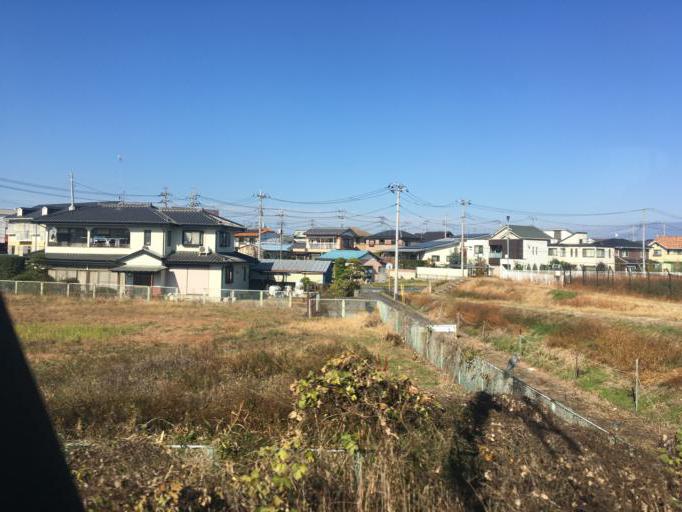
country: JP
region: Gunma
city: Isesaki
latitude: 36.3337
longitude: 139.2139
